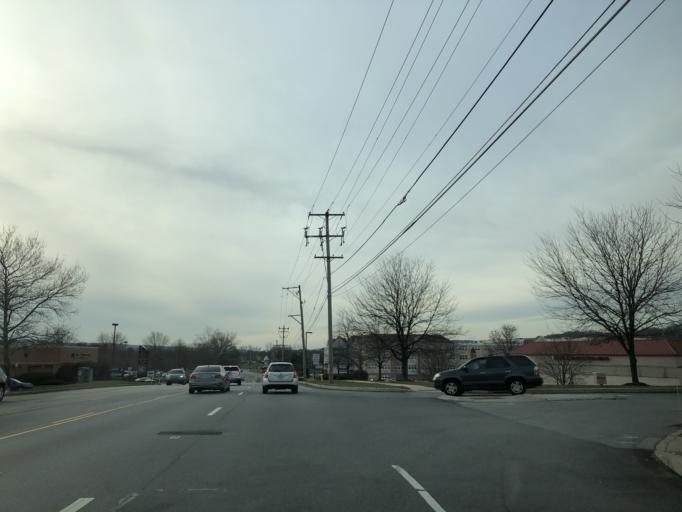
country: US
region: Pennsylvania
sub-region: Chester County
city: Downingtown
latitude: 40.0185
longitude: -75.6784
